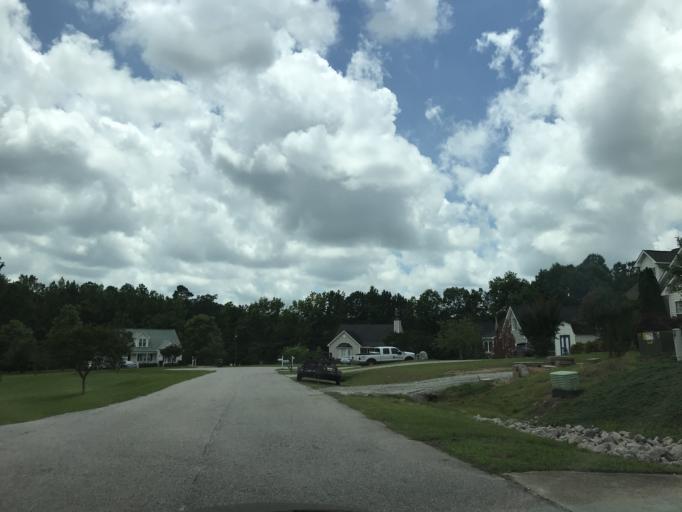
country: US
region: North Carolina
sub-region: Wake County
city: Rolesville
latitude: 35.9482
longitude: -78.3743
